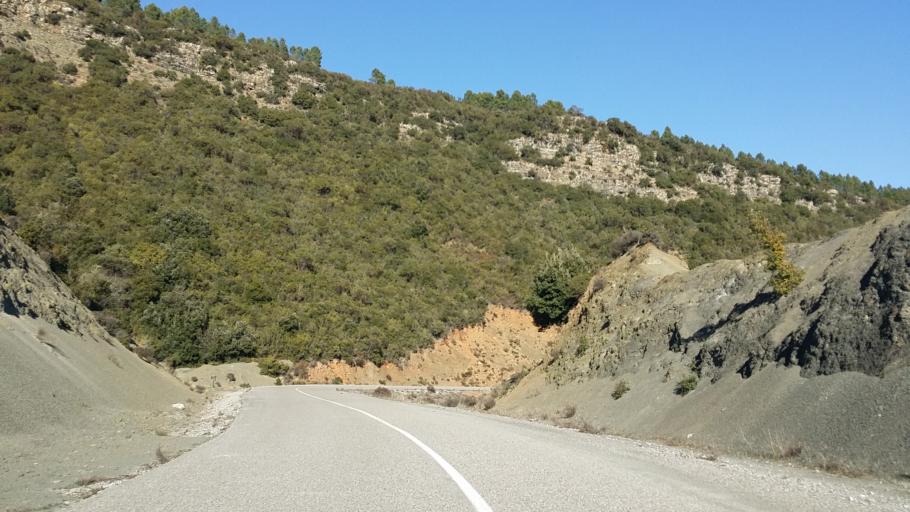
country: GR
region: Central Greece
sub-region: Nomos Evrytanias
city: Kerasochori
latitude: 38.9873
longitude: 21.5006
